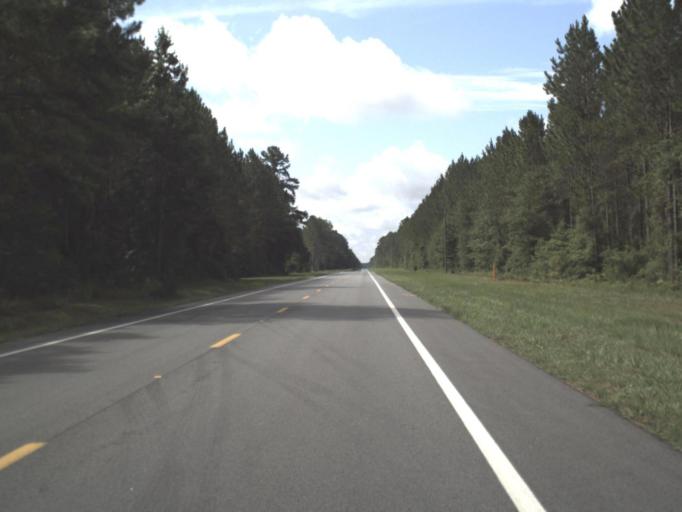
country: US
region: Florida
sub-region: Columbia County
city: Five Points
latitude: 30.4003
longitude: -82.6319
